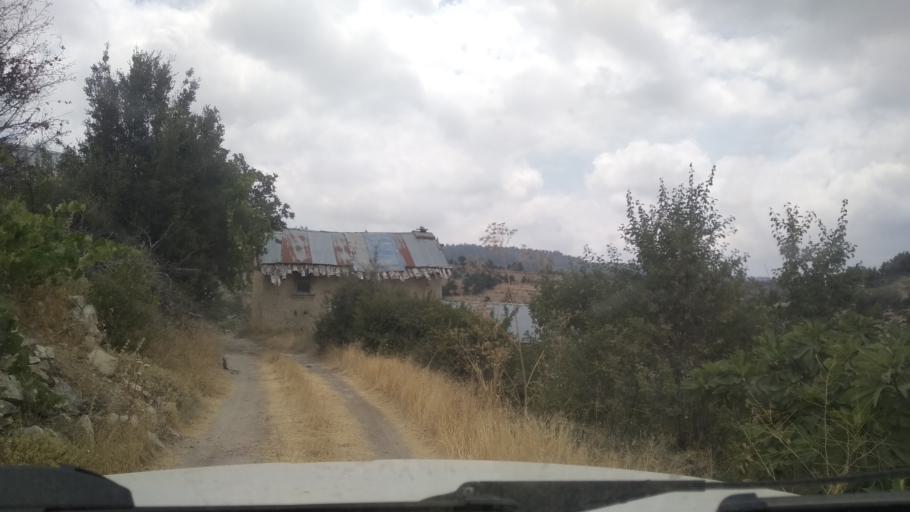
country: TR
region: Mersin
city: Sarikavak
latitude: 36.5989
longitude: 33.7276
